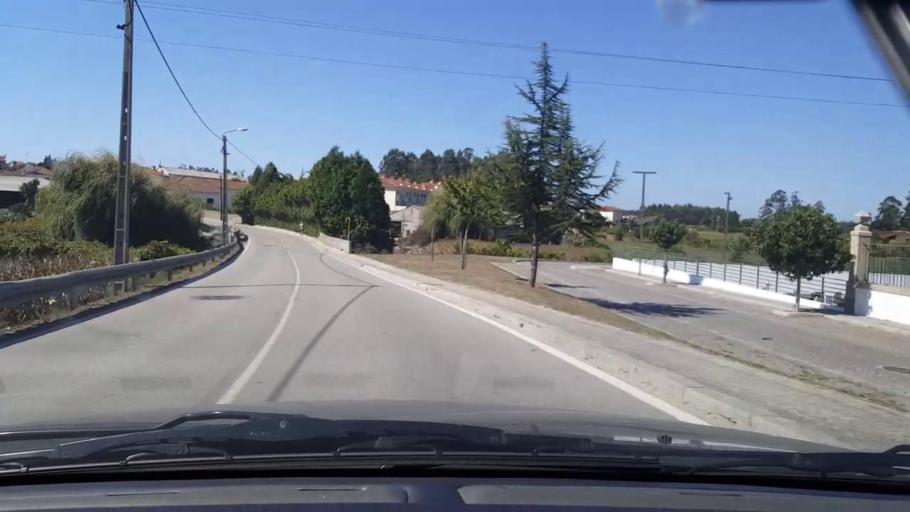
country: PT
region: Porto
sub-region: Vila do Conde
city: Arvore
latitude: 41.3418
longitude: -8.6688
